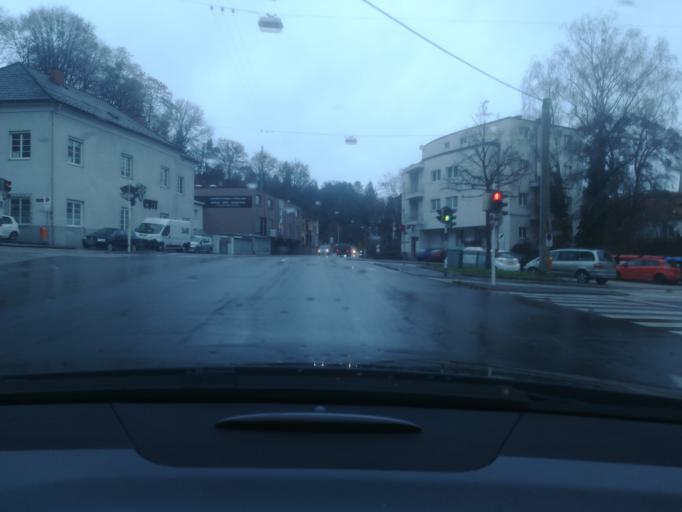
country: AT
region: Upper Austria
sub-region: Linz Stadt
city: Linz
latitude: 48.2934
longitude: 14.2852
